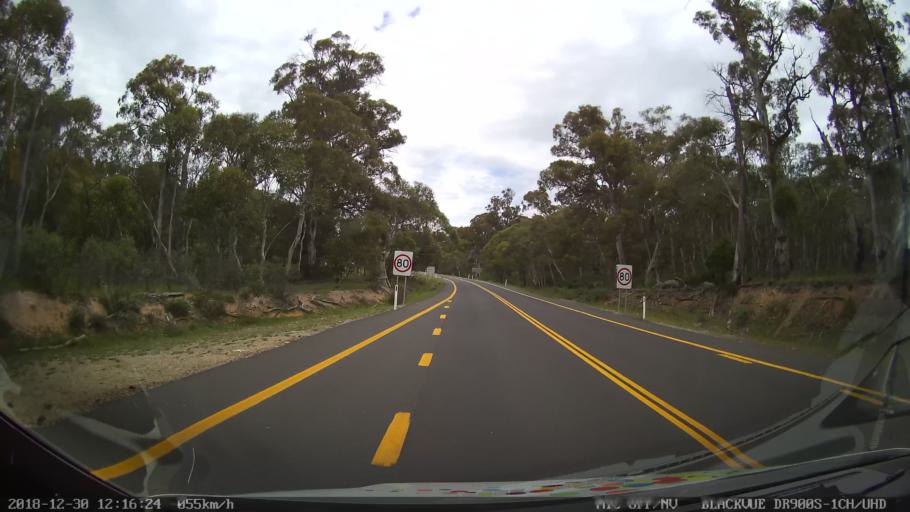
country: AU
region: New South Wales
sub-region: Snowy River
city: Jindabyne
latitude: -36.3456
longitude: 148.5664
